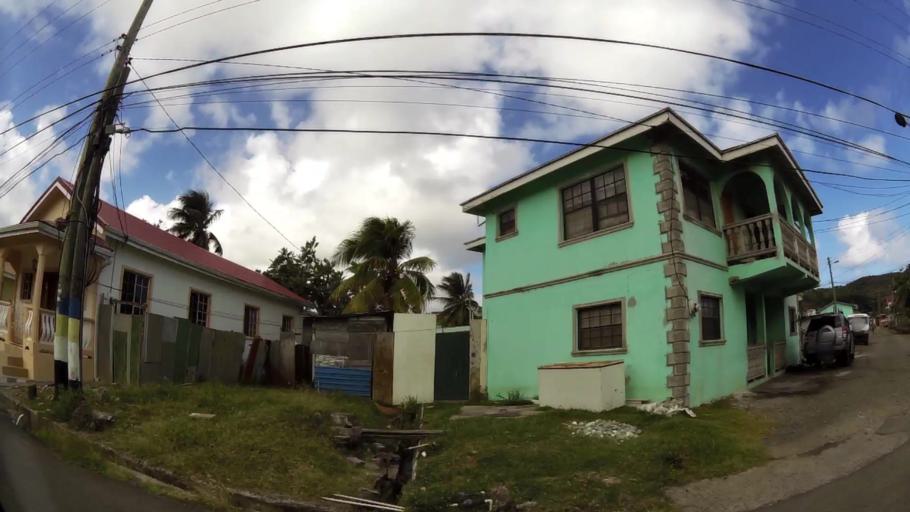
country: LC
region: Dennery Quarter
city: Dennery
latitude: 13.9087
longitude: -60.8921
